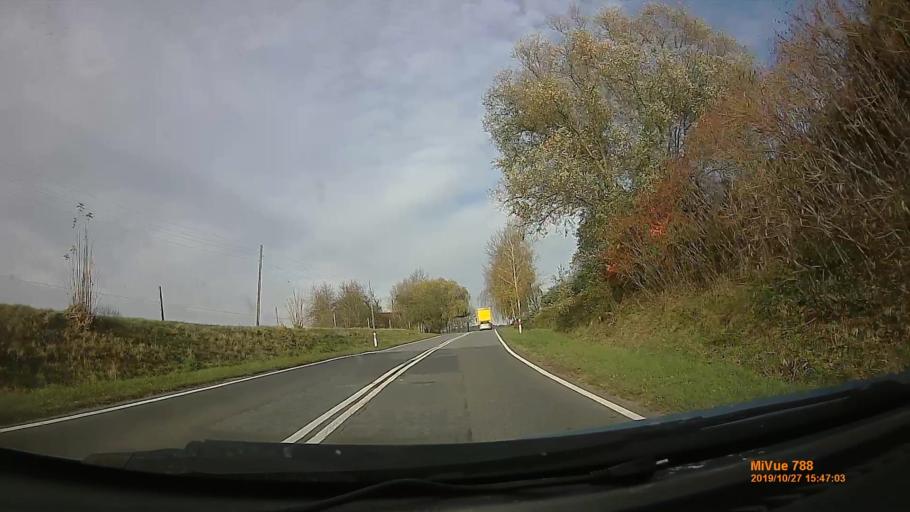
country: PL
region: Lower Silesian Voivodeship
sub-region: Powiat klodzki
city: Bozkow
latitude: 50.4864
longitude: 16.5830
